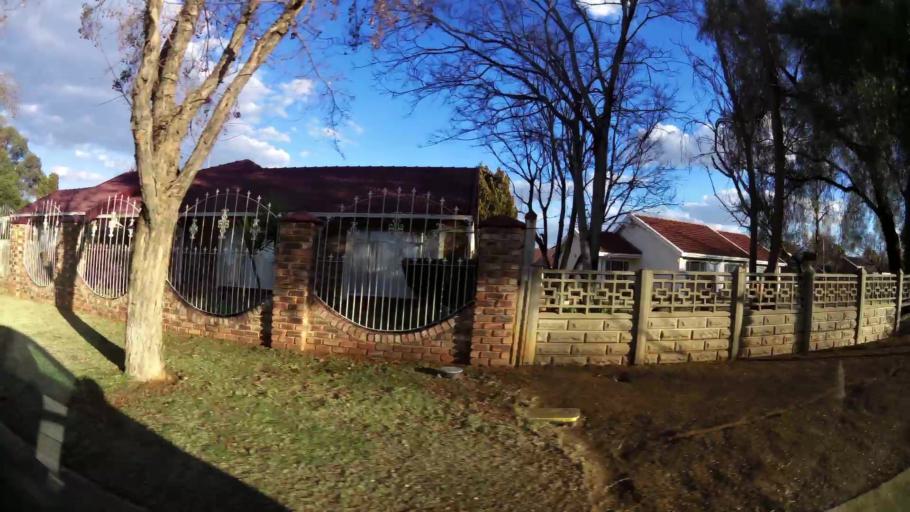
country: ZA
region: North-West
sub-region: Dr Kenneth Kaunda District Municipality
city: Potchefstroom
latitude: -26.7371
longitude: 27.0955
